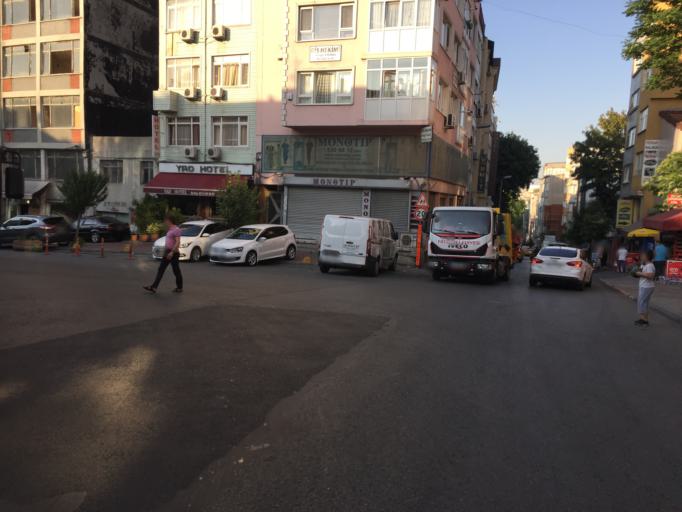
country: TR
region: Istanbul
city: Istanbul
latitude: 41.0081
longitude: 28.9454
